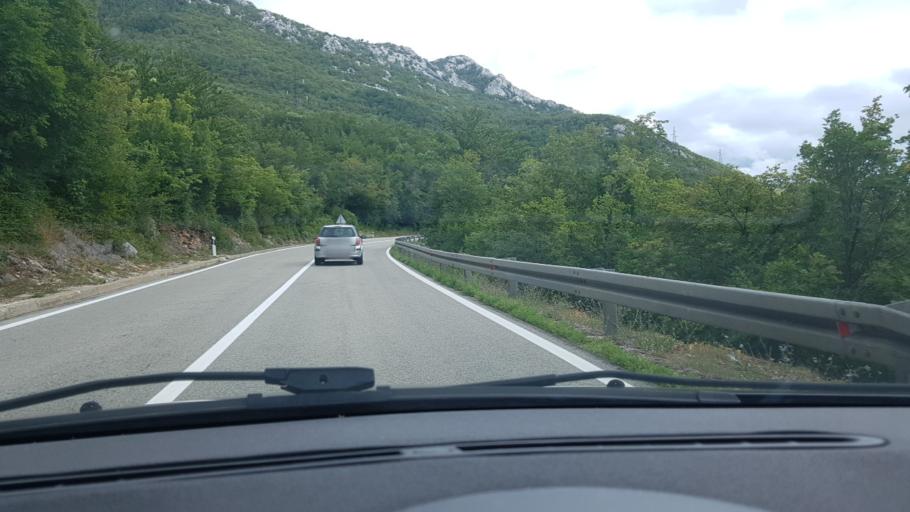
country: HR
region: Zadarska
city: Gracac
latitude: 44.2648
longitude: 15.8125
